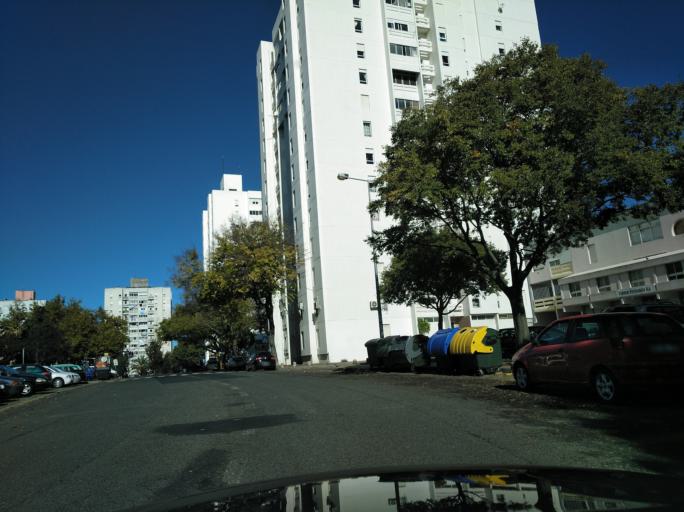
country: PT
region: Lisbon
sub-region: Loures
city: Moscavide
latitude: 38.7457
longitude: -9.1129
